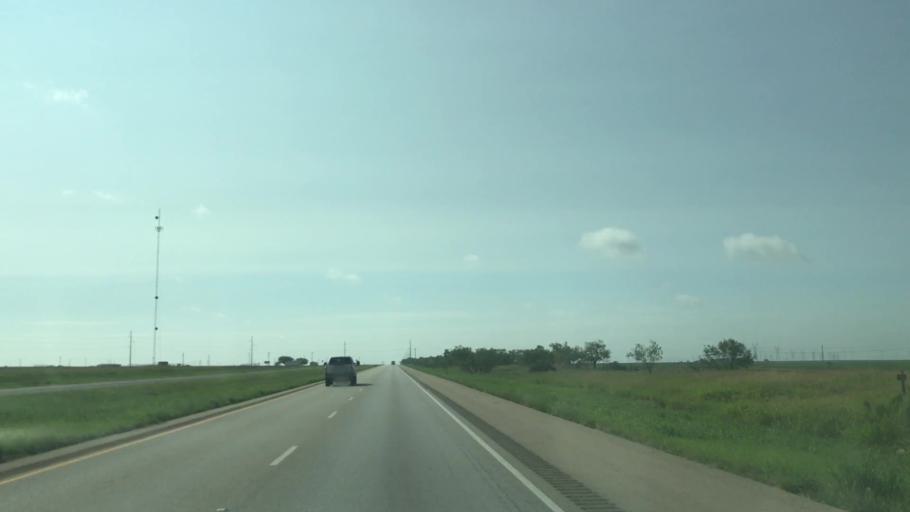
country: US
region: Texas
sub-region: Nolan County
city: Roscoe
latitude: 32.5666
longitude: -100.7118
